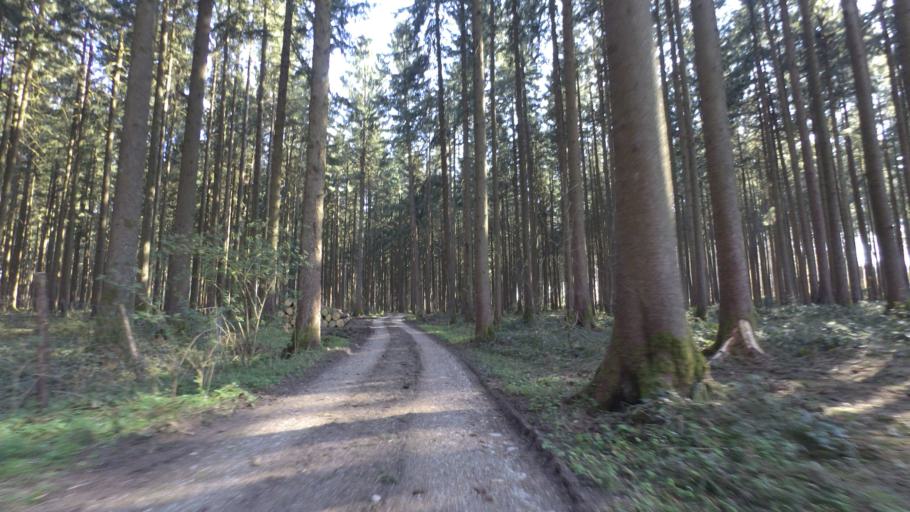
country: DE
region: Bavaria
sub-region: Upper Bavaria
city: Traunreut
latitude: 47.9368
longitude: 12.5762
